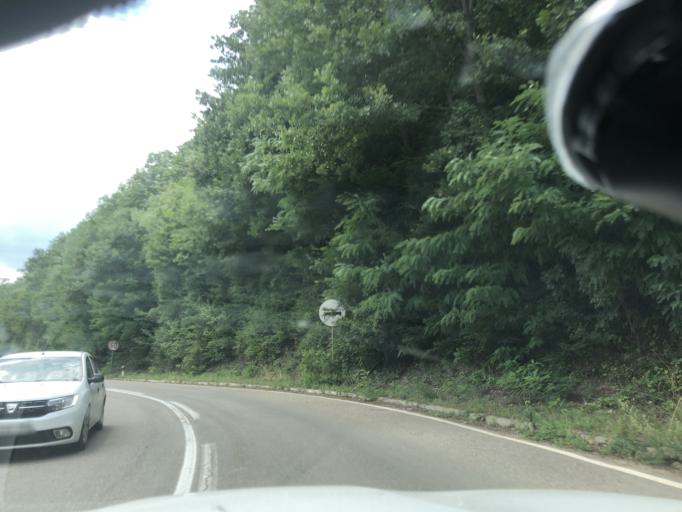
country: RS
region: Central Serbia
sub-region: Jablanicki Okrug
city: Medvega
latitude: 42.8172
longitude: 21.5817
